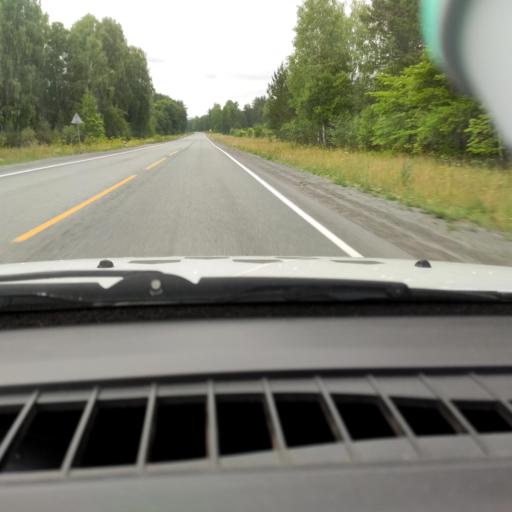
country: RU
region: Chelyabinsk
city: Turgoyak
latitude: 55.2985
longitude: 60.1981
